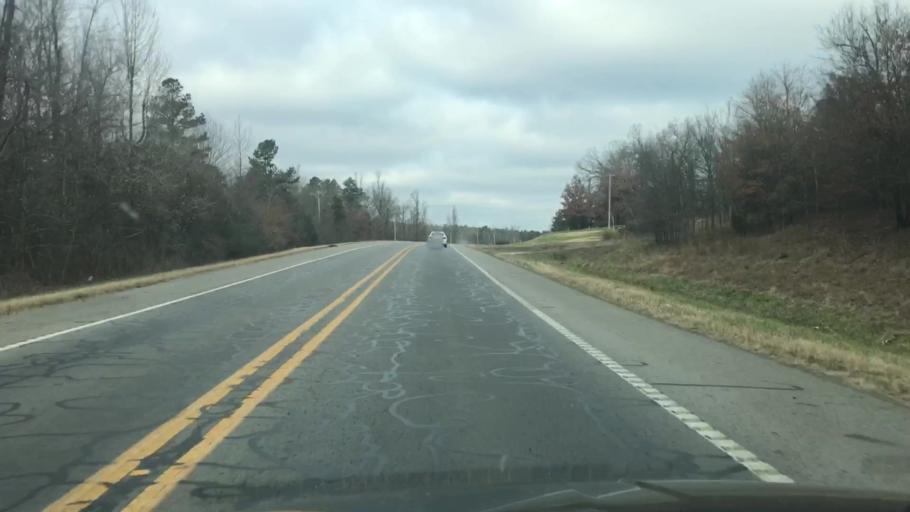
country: US
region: Arkansas
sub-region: Scott County
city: Waldron
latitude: 34.8248
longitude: -94.0372
